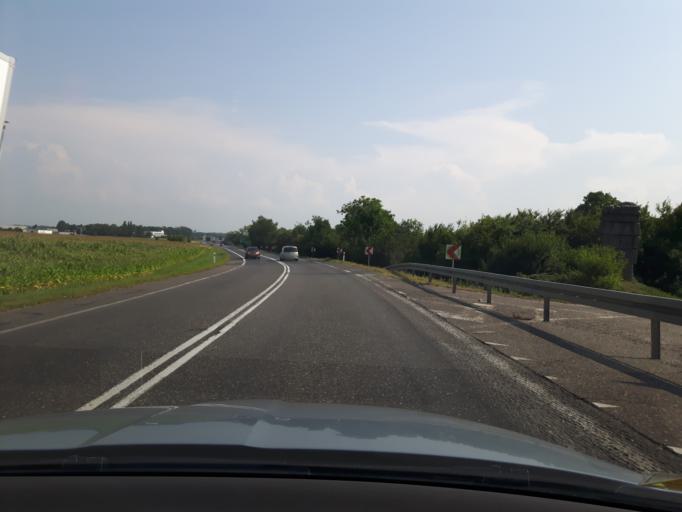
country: PL
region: Masovian Voivodeship
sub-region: Powiat plonski
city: Plonsk
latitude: 52.6401
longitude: 20.3730
